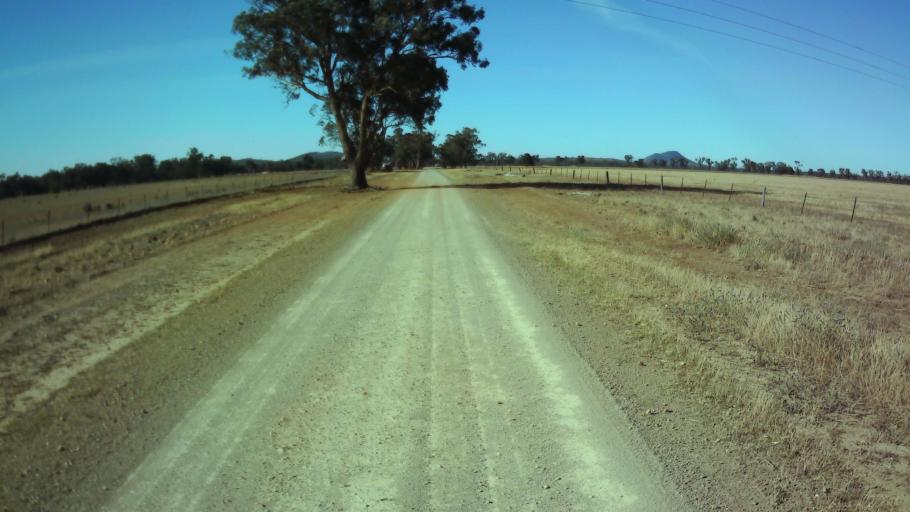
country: AU
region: New South Wales
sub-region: Weddin
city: Grenfell
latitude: -33.8443
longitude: 147.8766
